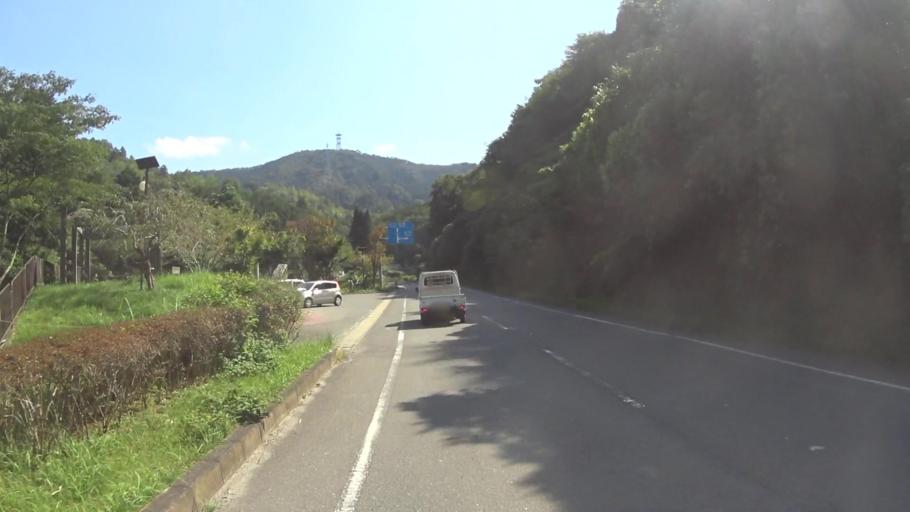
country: JP
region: Kyoto
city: Kameoka
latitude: 34.9711
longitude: 135.5711
